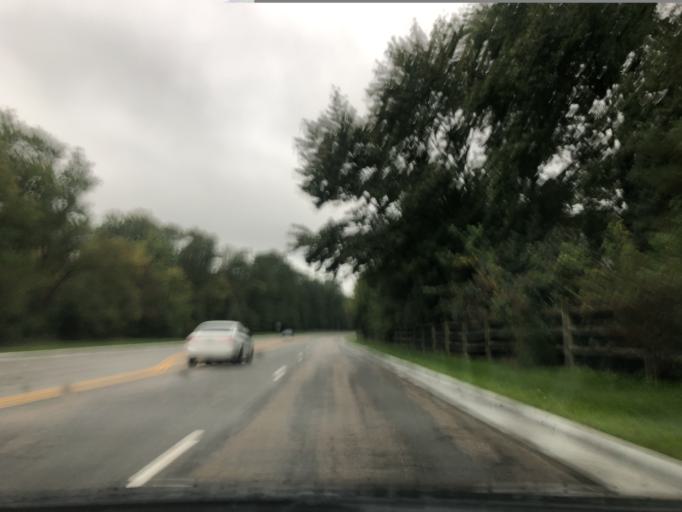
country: US
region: Ohio
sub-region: Hamilton County
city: Blue Ash
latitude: 39.2369
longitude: -84.3914
